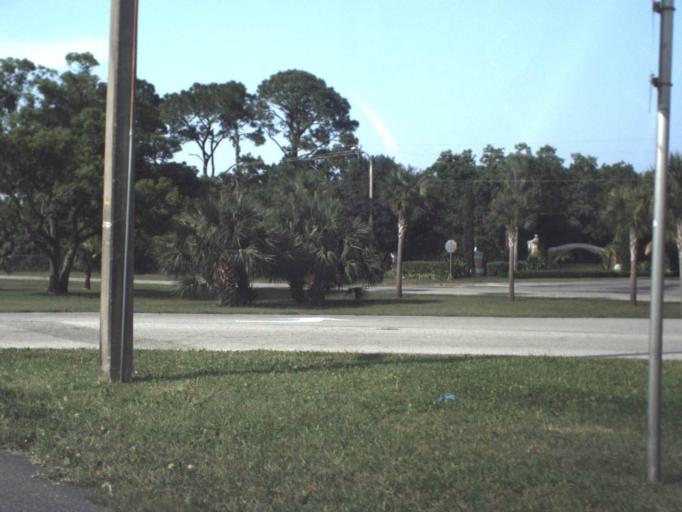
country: US
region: Florida
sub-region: Saint Johns County
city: Villano Beach
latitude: 29.9224
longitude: -81.3249
